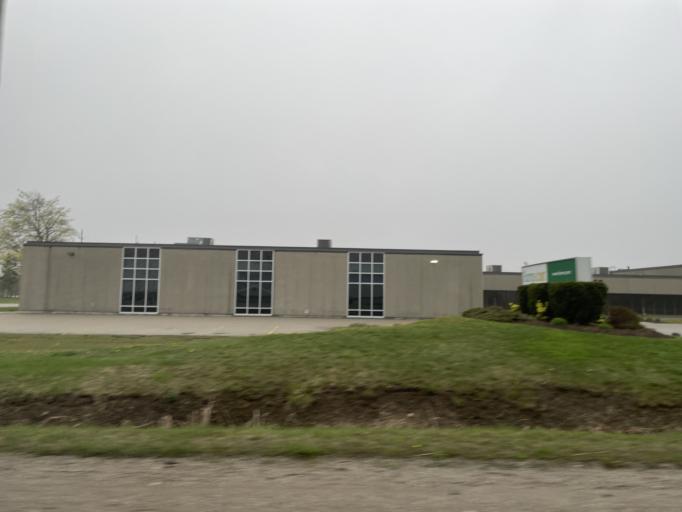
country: CA
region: Ontario
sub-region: Wellington County
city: Guelph
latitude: 43.5436
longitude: -80.2993
